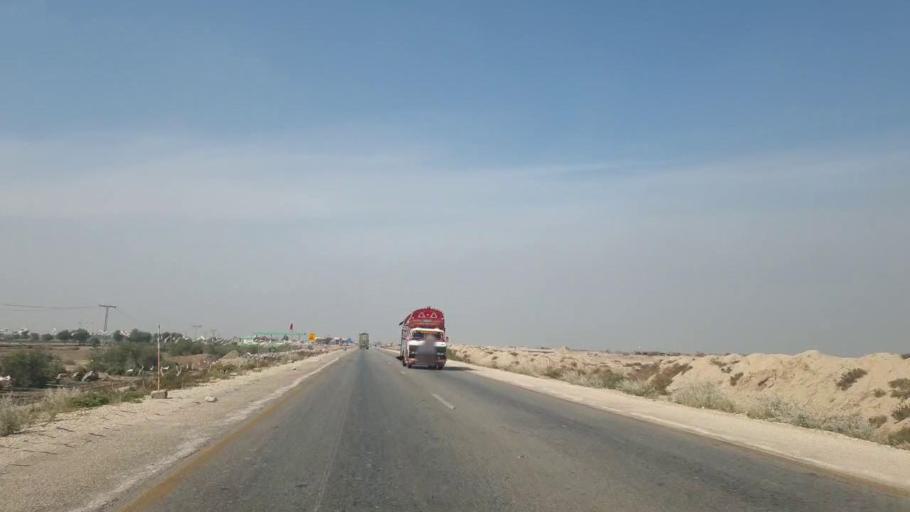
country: PK
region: Sindh
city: Sann
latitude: 25.9485
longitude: 68.1986
